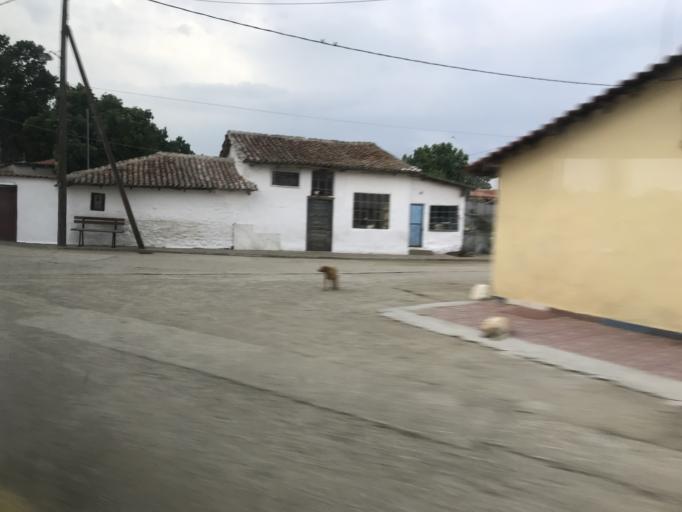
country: GR
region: East Macedonia and Thrace
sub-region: Nomos Rodopis
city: Aratos
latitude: 41.0805
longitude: 25.5548
